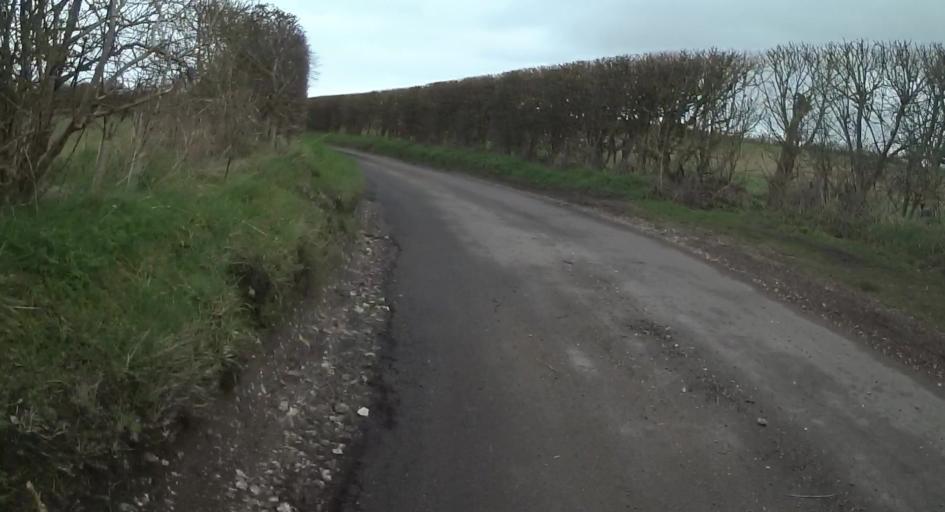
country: GB
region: England
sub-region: Hampshire
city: Kingsclere
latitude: 51.2822
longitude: -1.2212
